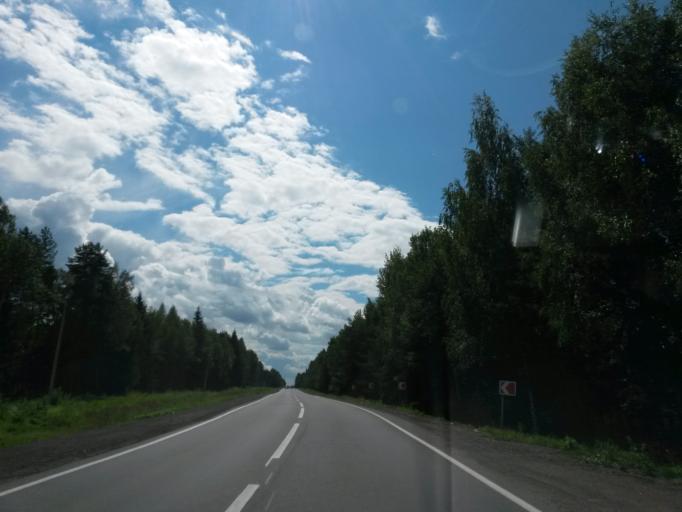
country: RU
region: Jaroslavl
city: Gavrilov-Yam
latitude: 57.2782
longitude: 39.9513
